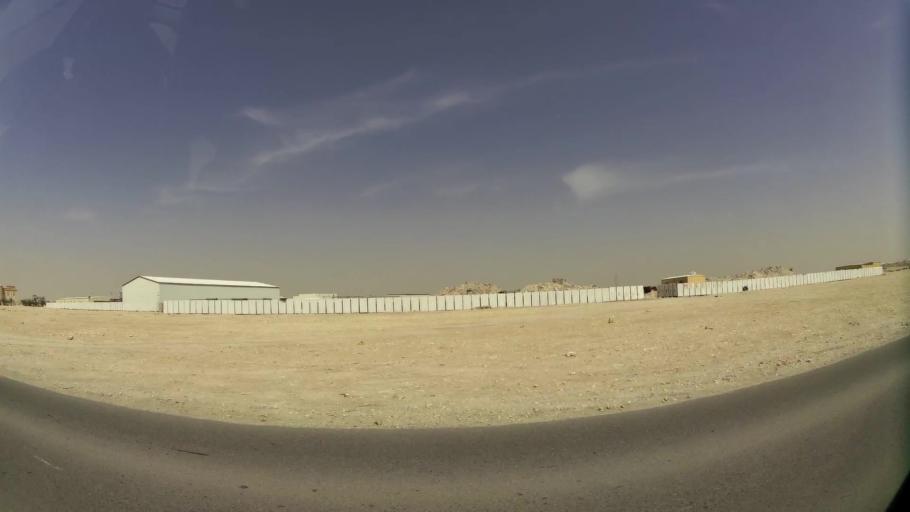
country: QA
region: Baladiyat ar Rayyan
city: Ar Rayyan
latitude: 25.2620
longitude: 51.3812
